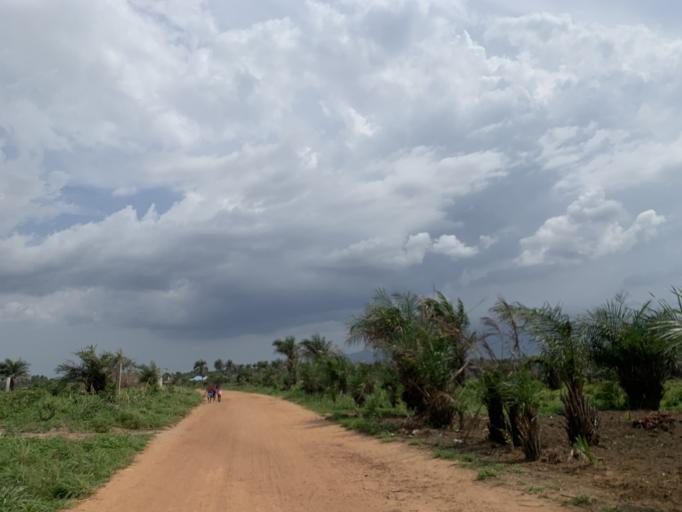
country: SL
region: Western Area
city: Waterloo
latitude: 8.3549
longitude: -13.0489
